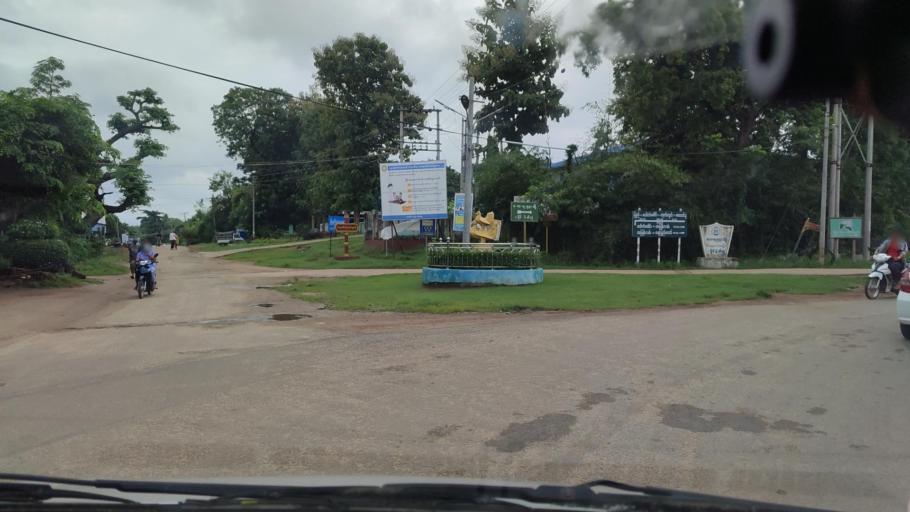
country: MM
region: Bago
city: Pyay
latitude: 18.9101
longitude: 95.5538
